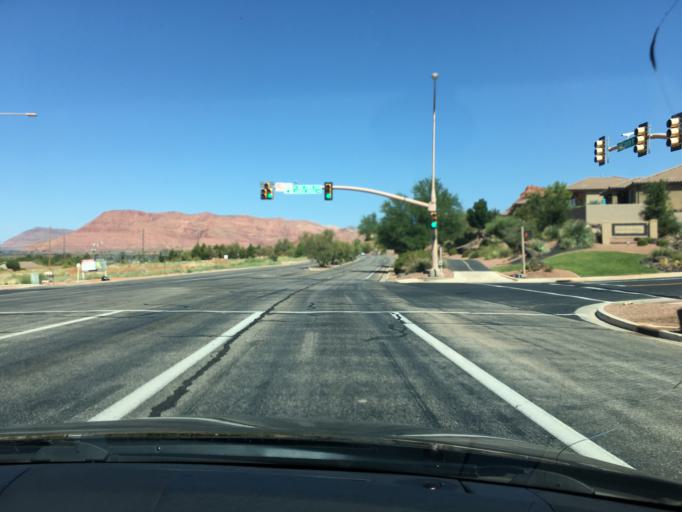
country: US
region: Utah
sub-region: Washington County
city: Santa Clara
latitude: 37.1411
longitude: -113.6217
